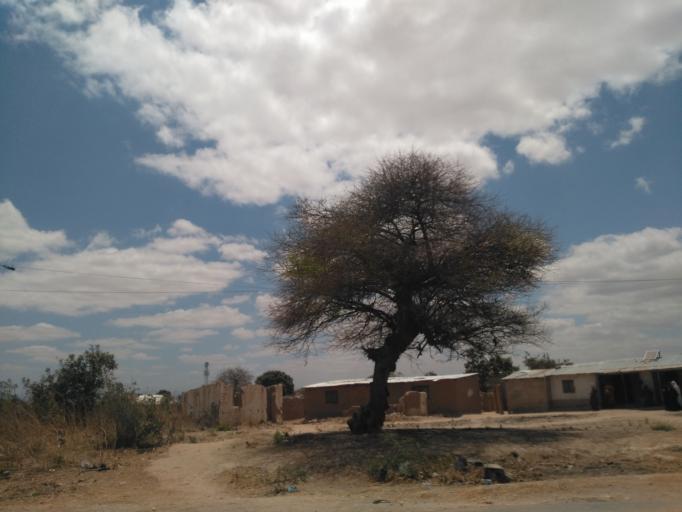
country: TZ
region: Dodoma
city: Kisasa
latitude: -6.1715
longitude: 35.7944
